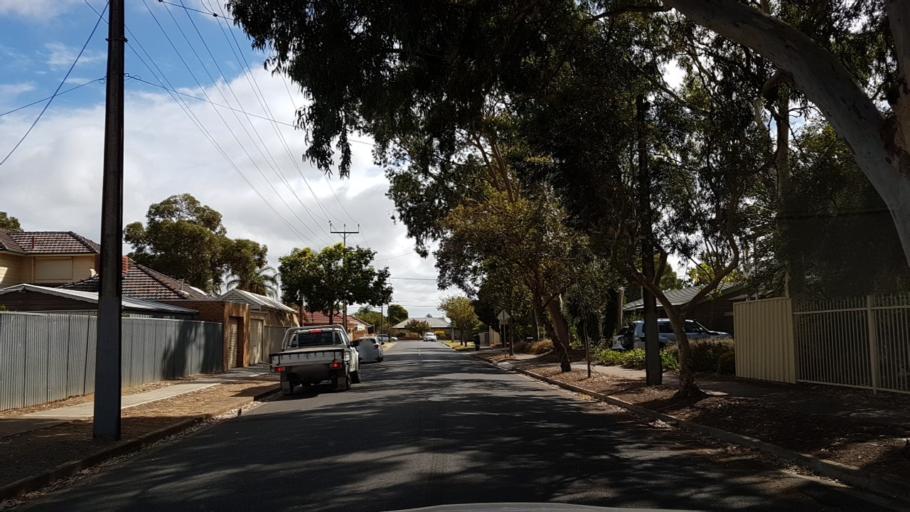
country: AU
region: South Australia
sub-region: Marion
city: Plympton Park
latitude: -34.9916
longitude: 138.5511
